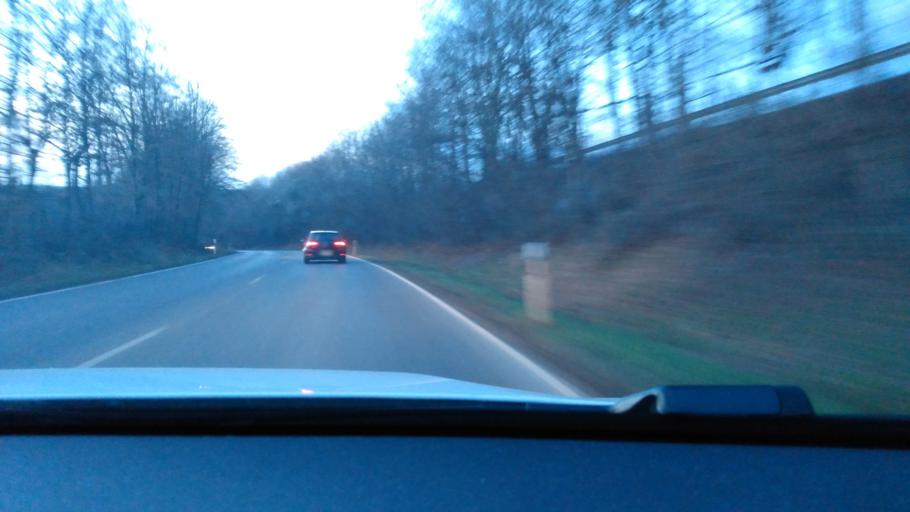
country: DE
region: North Rhine-Westphalia
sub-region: Regierungsbezirk Koln
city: Wachtberg
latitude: 50.6410
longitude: 7.1072
